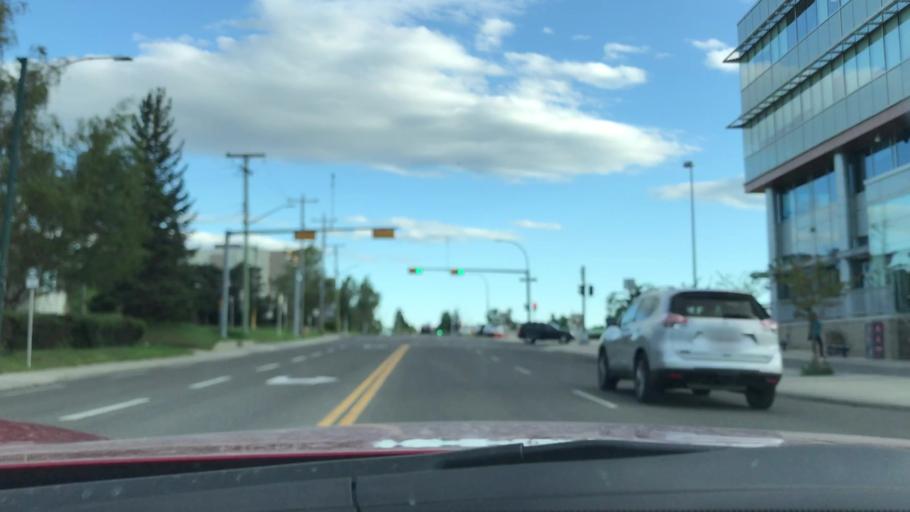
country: CA
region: Alberta
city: Calgary
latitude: 51.0407
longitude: -114.1355
